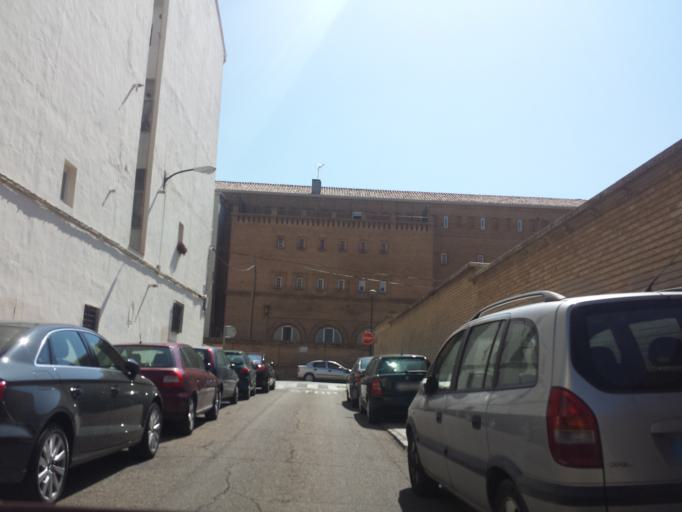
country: ES
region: Aragon
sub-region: Provincia de Zaragoza
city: Zaragoza
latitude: 41.6345
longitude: -0.8876
